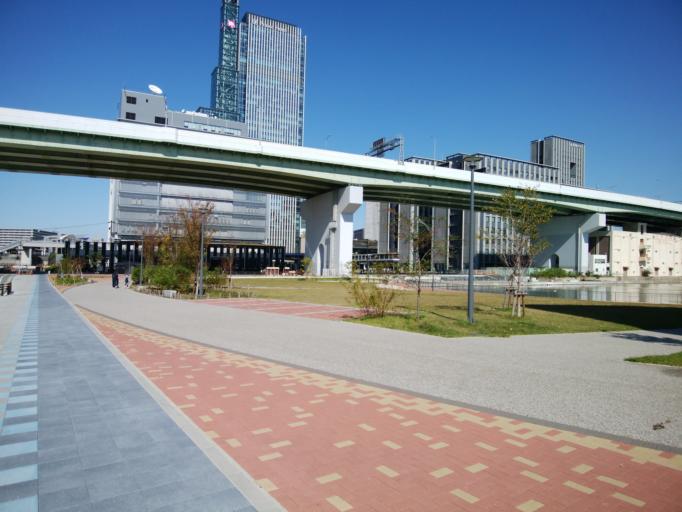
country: JP
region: Aichi
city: Nagoya-shi
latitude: 35.1591
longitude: 136.8829
